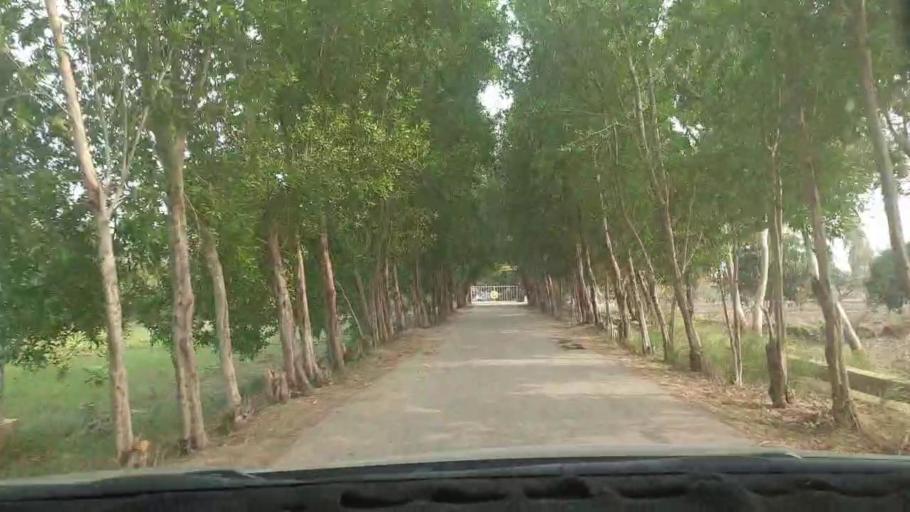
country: PK
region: Sindh
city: Jamshoro
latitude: 25.5056
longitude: 68.3161
